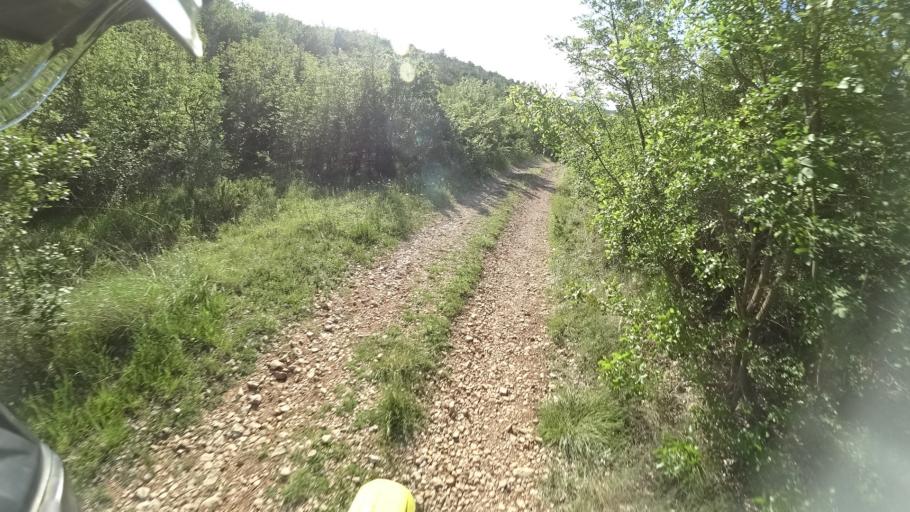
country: HR
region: Sibensko-Kniniska
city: Drnis
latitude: 43.8140
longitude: 16.0284
